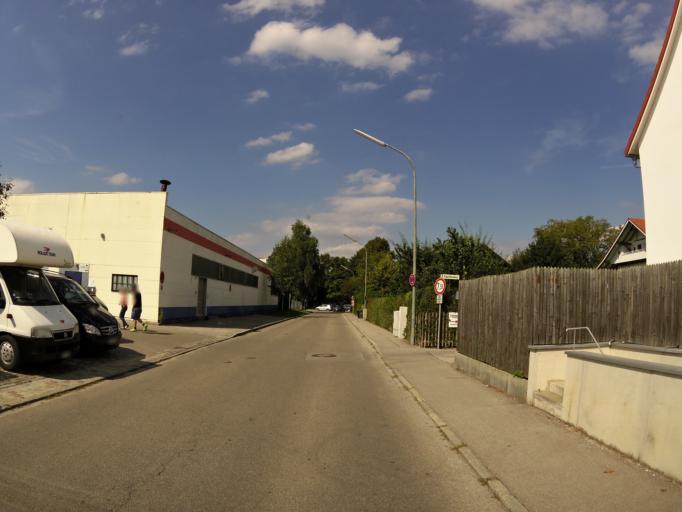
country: DE
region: Bavaria
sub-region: Upper Bavaria
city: Herrsching am Ammersee
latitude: 48.0003
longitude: 11.1715
